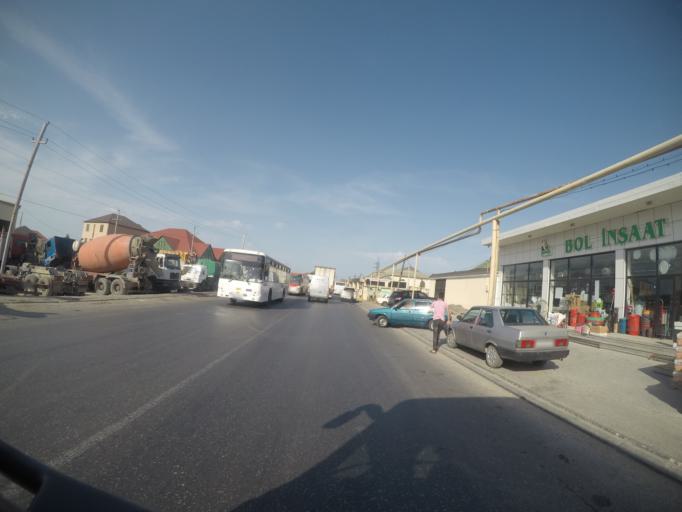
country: AZ
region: Baki
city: Bilajari
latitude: 40.4463
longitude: 49.7966
